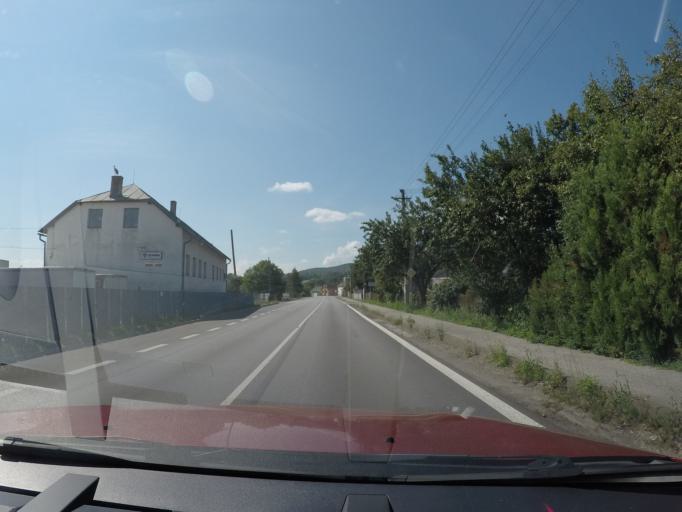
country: SK
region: Presovsky
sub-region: Okres Presov
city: Presov
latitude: 48.8787
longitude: 21.2463
